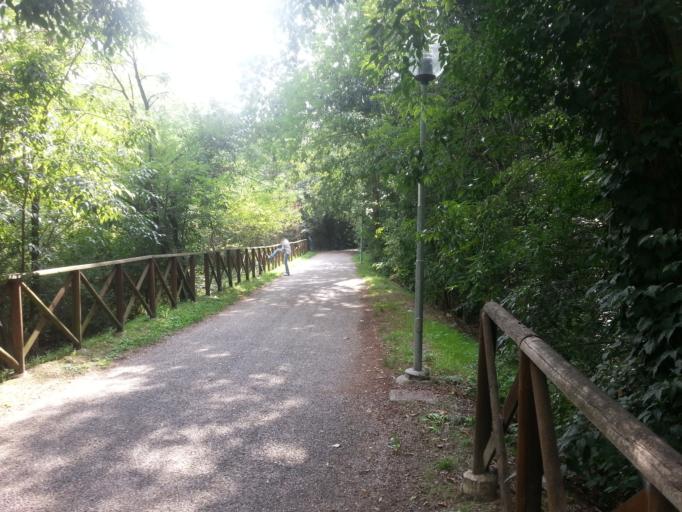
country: IT
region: Emilia-Romagna
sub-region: Provincia di Reggio Emilia
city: Reggio nell'Emilia
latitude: 44.6811
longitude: 10.6237
